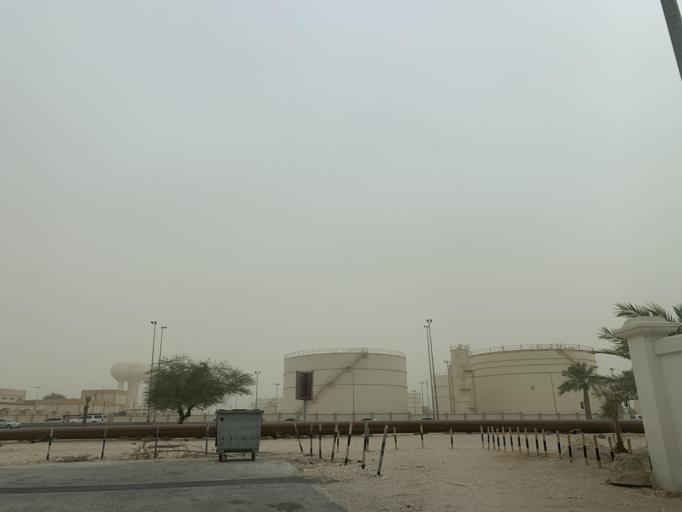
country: BH
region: Northern
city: Ar Rifa'
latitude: 26.1353
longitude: 50.5348
